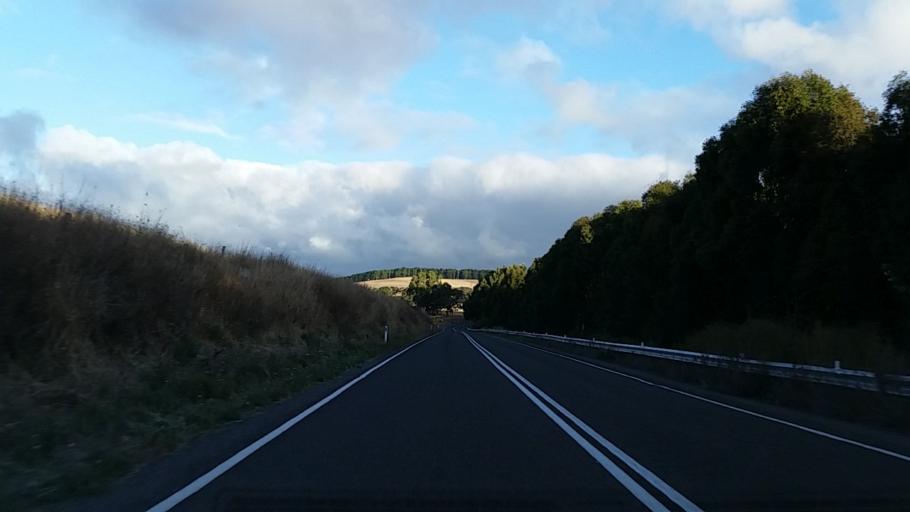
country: AU
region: South Australia
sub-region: Yankalilla
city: Normanville
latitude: -35.5592
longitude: 138.1988
